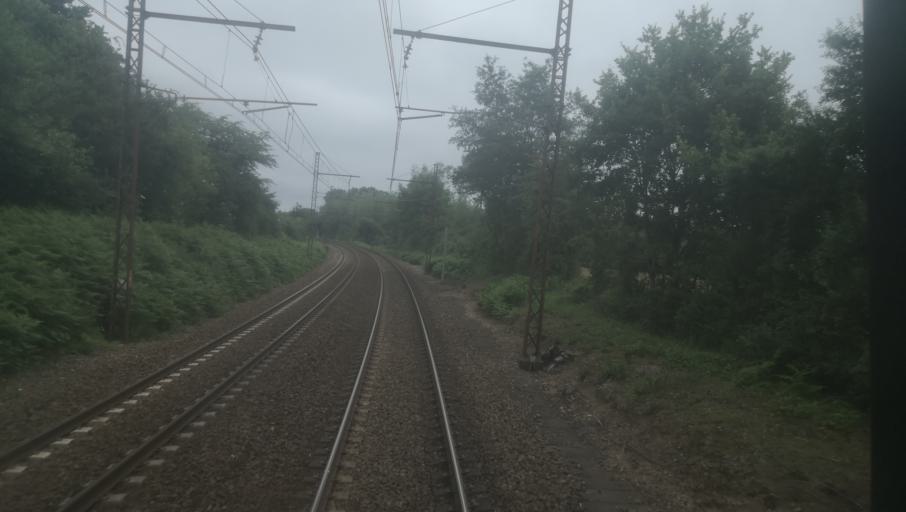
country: FR
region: Limousin
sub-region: Departement de la Creuse
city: La Souterraine
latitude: 46.2294
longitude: 1.4966
